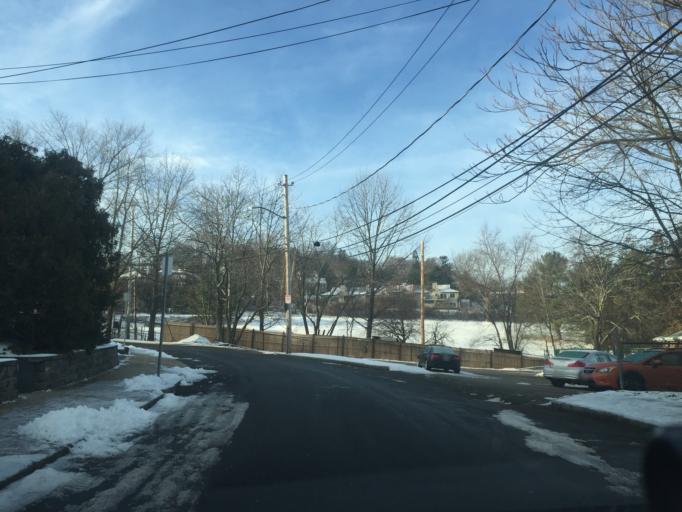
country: US
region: Massachusetts
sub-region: Middlesex County
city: Watertown
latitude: 42.3428
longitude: -71.1681
